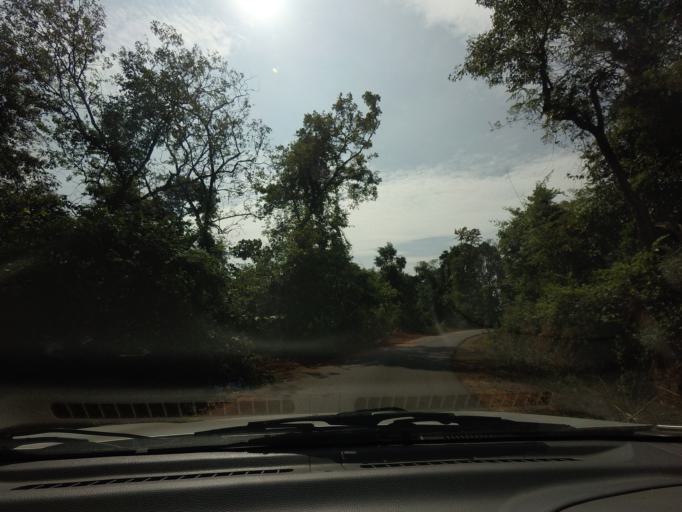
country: IN
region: Karnataka
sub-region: Kodagu
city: Somvarpet
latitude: 12.6870
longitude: 75.6158
